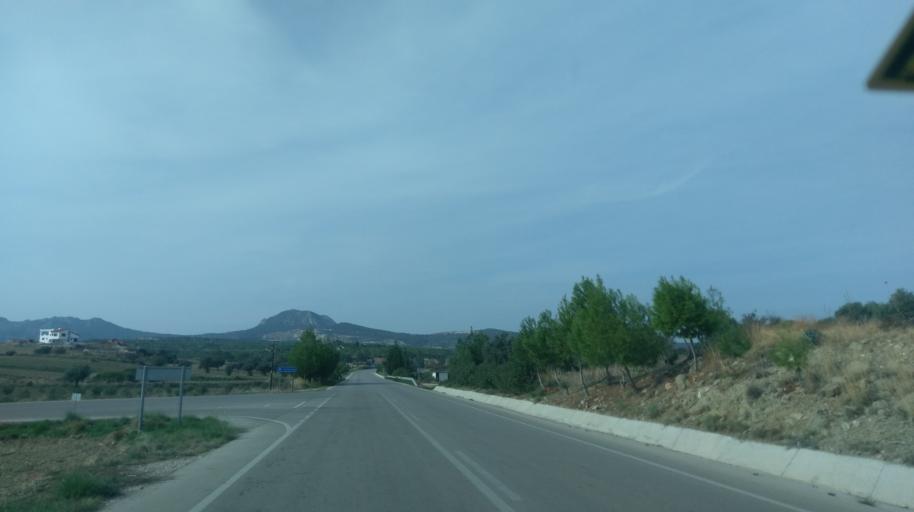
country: CY
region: Ammochostos
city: Trikomo
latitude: 35.4003
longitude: 33.9969
